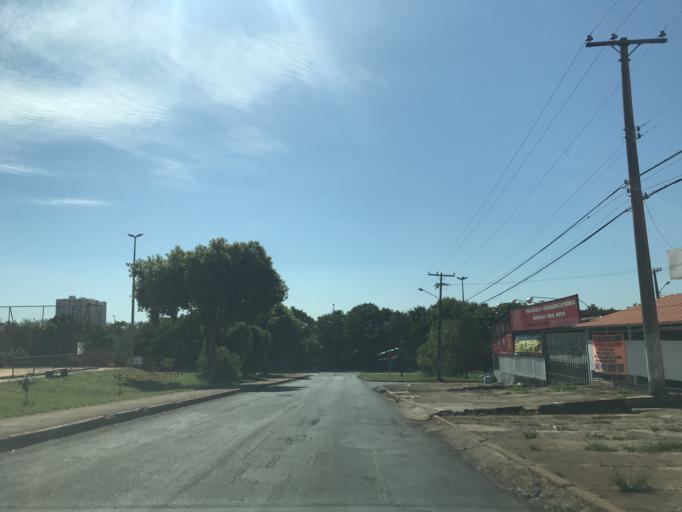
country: BR
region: Federal District
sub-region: Brasilia
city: Brasilia
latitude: -15.8173
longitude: -48.0792
